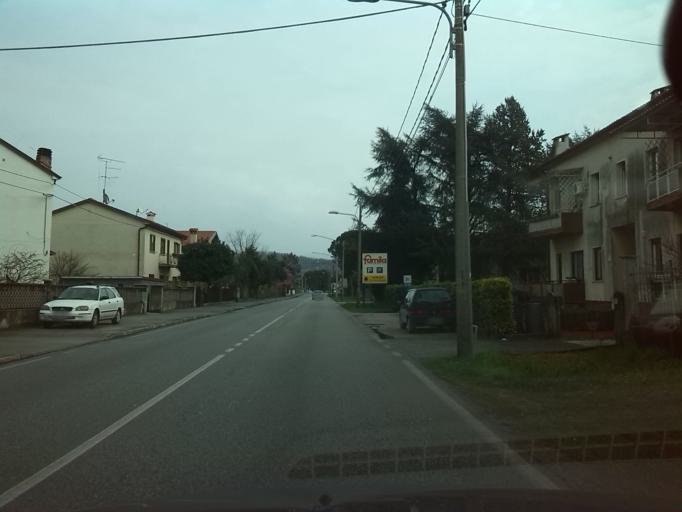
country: IT
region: Friuli Venezia Giulia
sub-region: Provincia di Gorizia
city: Mossa
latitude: 45.9356
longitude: 13.5555
